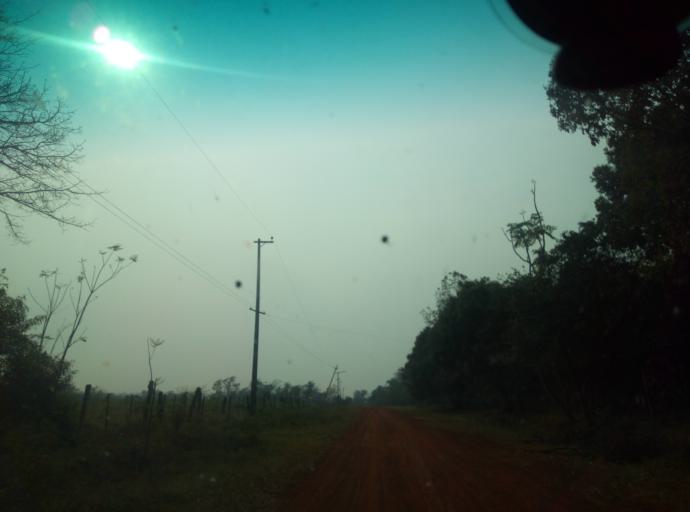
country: PY
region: Caaguazu
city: Carayao
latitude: -25.2037
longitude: -56.2283
